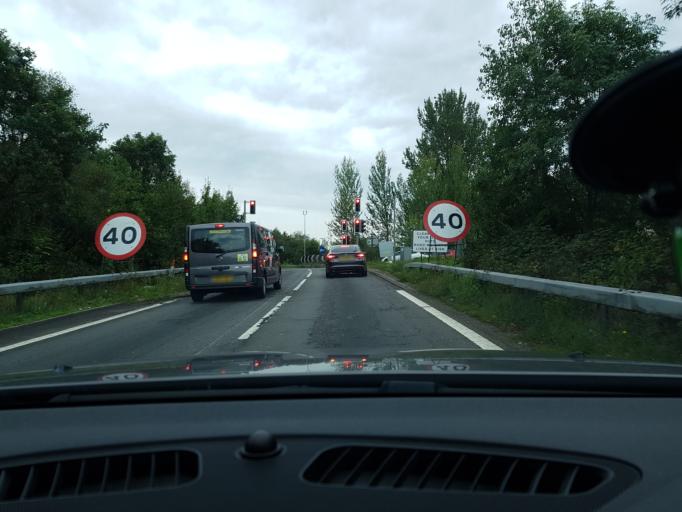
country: GB
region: England
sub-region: West Sussex
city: Copthorne
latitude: 51.1597
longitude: -0.1335
